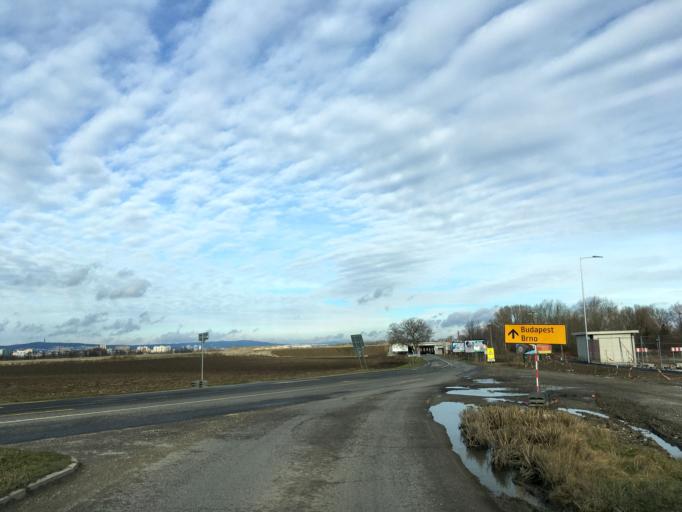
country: AT
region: Burgenland
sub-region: Politischer Bezirk Neusiedl am See
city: Deutsch Jahrndorf
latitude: 48.0715
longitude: 17.1180
